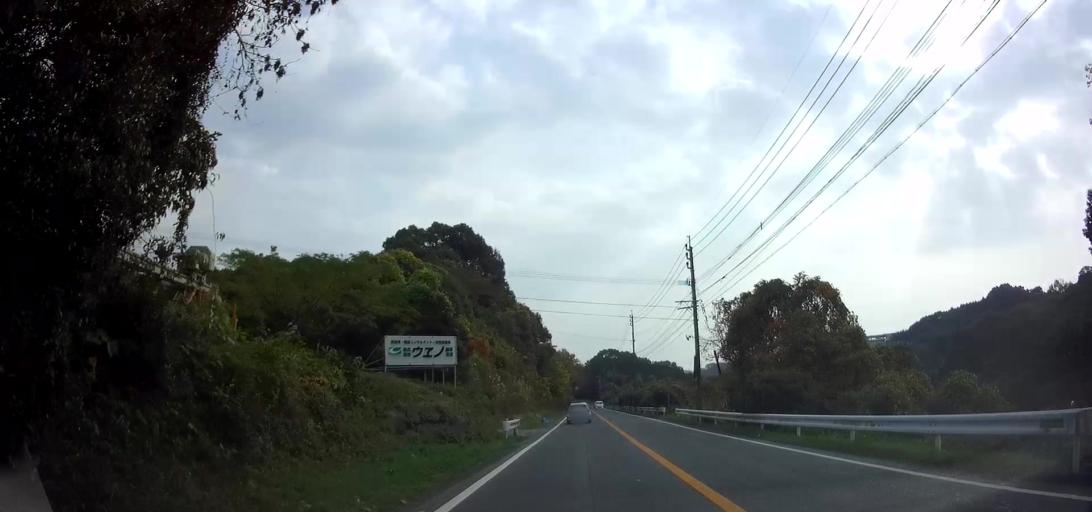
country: JP
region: Nagasaki
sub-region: Isahaya-shi
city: Isahaya
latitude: 32.7902
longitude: 130.0496
